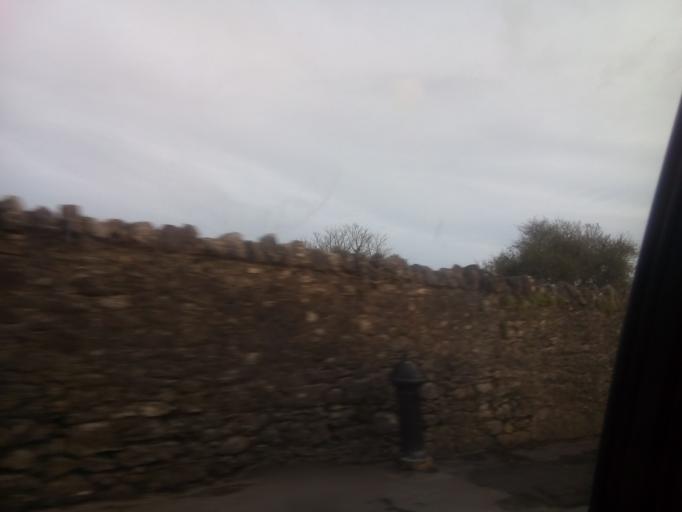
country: IE
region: Leinster
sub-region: Laois
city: Abbeyleix
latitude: 52.8439
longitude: -7.3983
